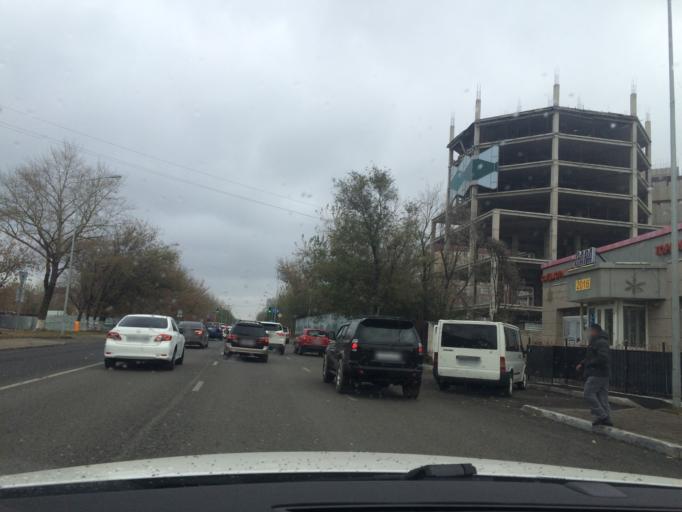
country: KZ
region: Astana Qalasy
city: Astana
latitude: 51.1707
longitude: 71.4487
